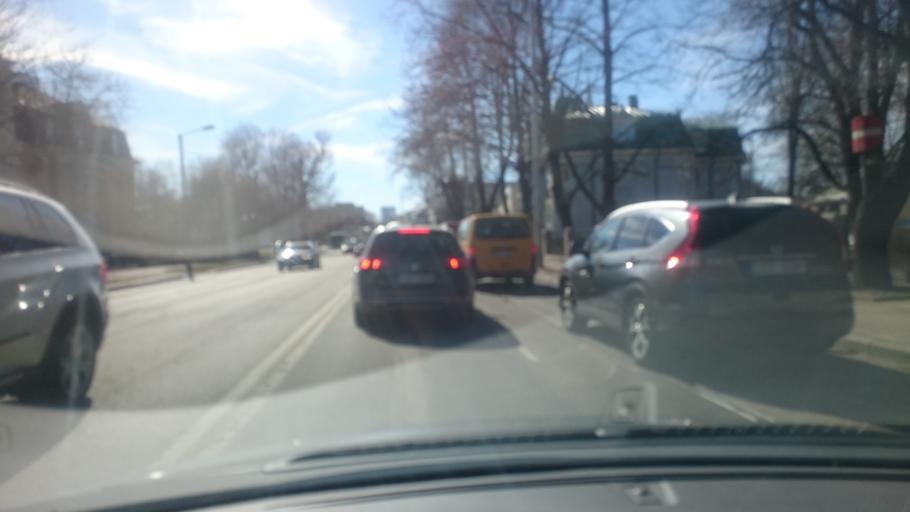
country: EE
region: Harju
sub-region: Tallinna linn
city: Tallinn
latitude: 59.4395
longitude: 24.7791
